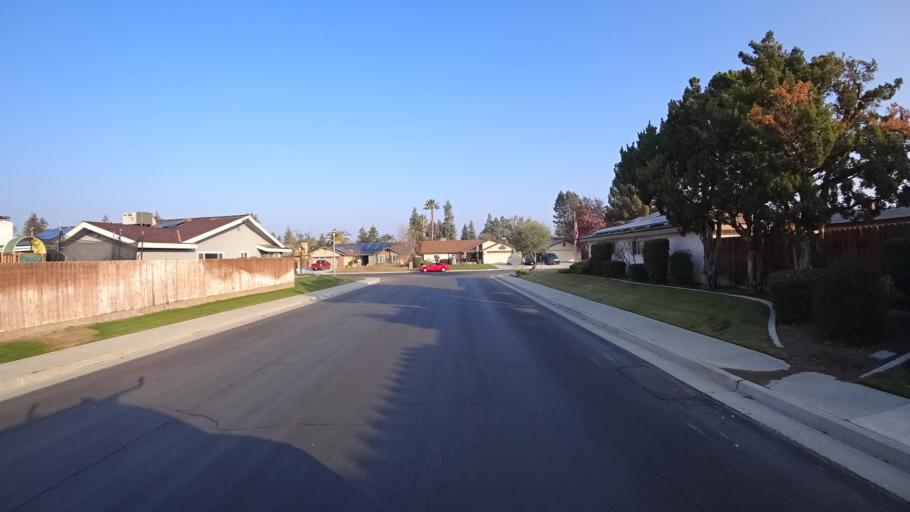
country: US
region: California
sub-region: Kern County
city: Greenacres
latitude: 35.3244
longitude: -119.0772
